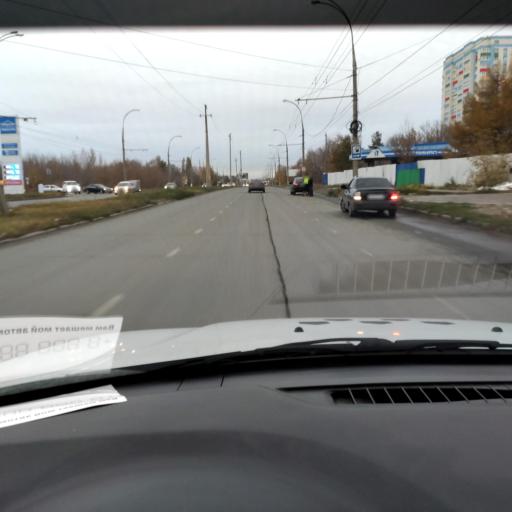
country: RU
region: Samara
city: Tol'yatti
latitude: 53.5398
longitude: 49.3001
